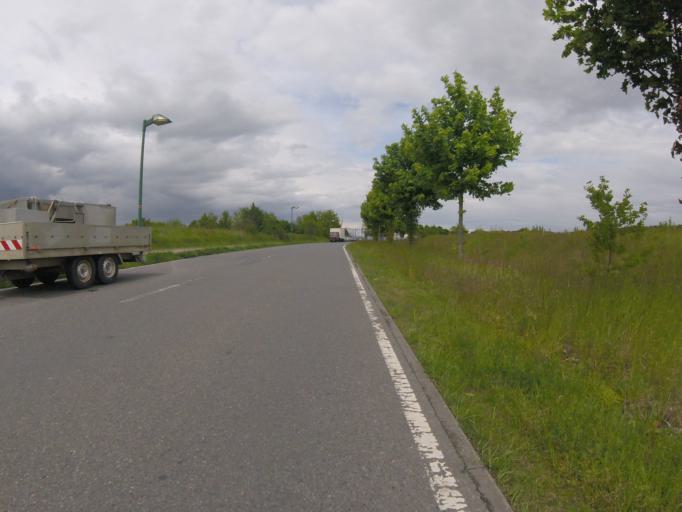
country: DE
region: Brandenburg
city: Konigs Wusterhausen
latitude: 52.3043
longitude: 13.5987
